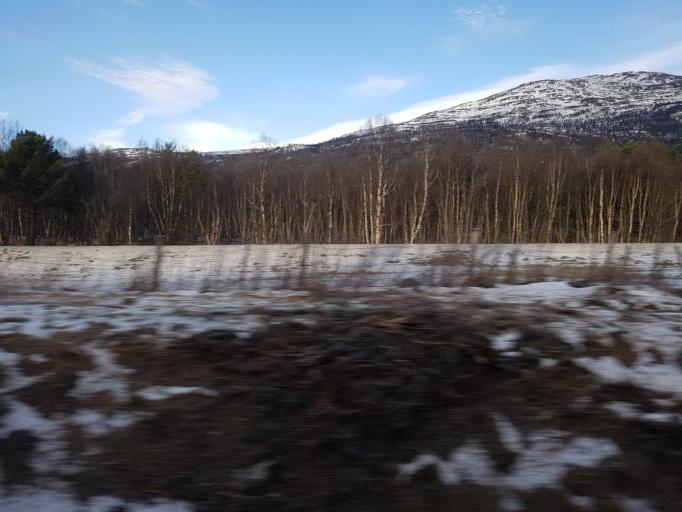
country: NO
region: Sor-Trondelag
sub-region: Oppdal
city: Oppdal
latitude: 62.6116
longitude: 9.7437
